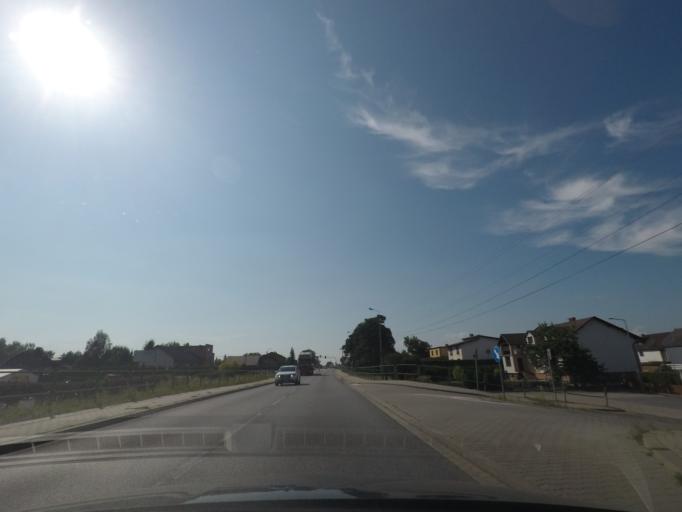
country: PL
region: Silesian Voivodeship
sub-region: Powiat pszczynski
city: Suszec
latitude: 50.0306
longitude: 18.7870
